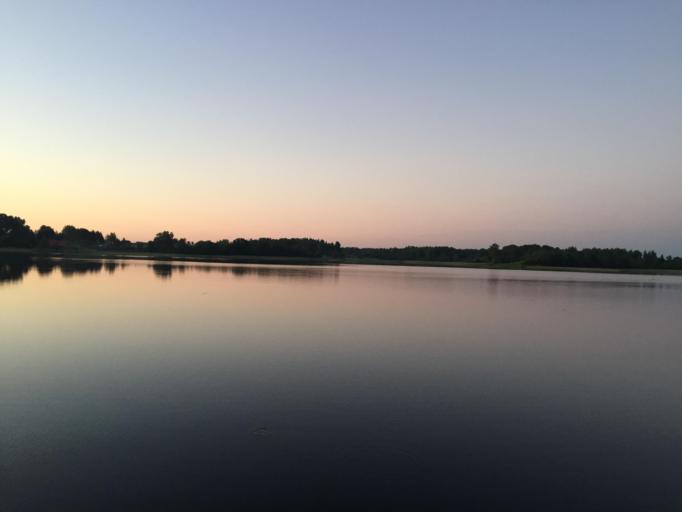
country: LV
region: Rezekne
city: Rezekne
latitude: 56.3686
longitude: 27.4168
